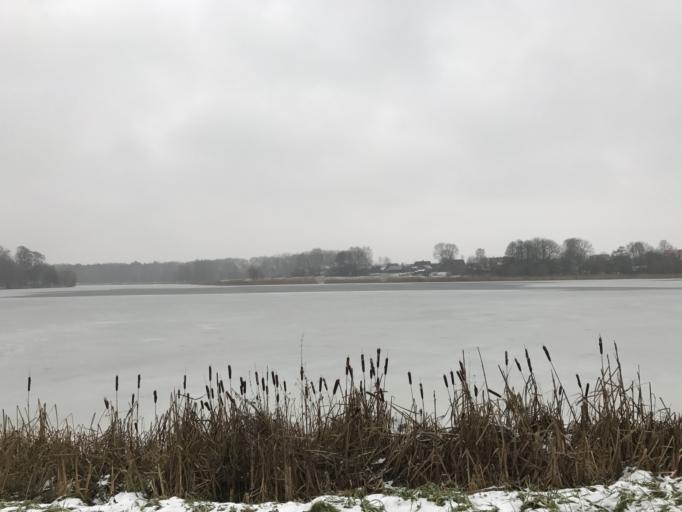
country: BY
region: Minsk
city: Nyasvizh
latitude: 53.2201
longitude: 26.6862
